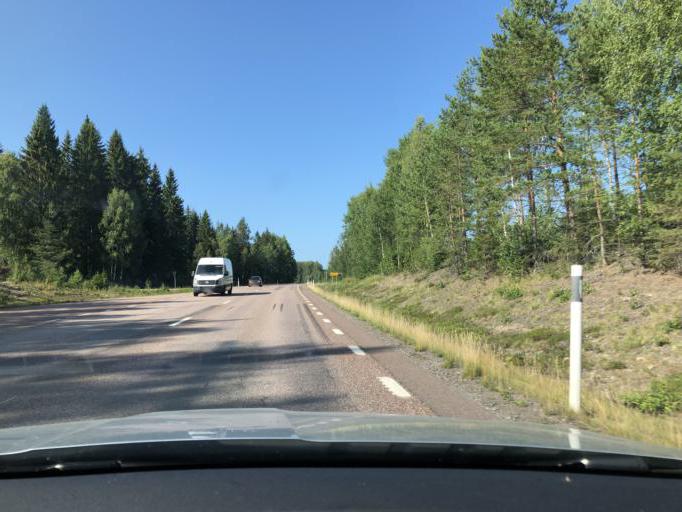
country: SE
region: Dalarna
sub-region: Saters Kommun
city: Saeter
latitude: 60.4634
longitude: 15.7999
